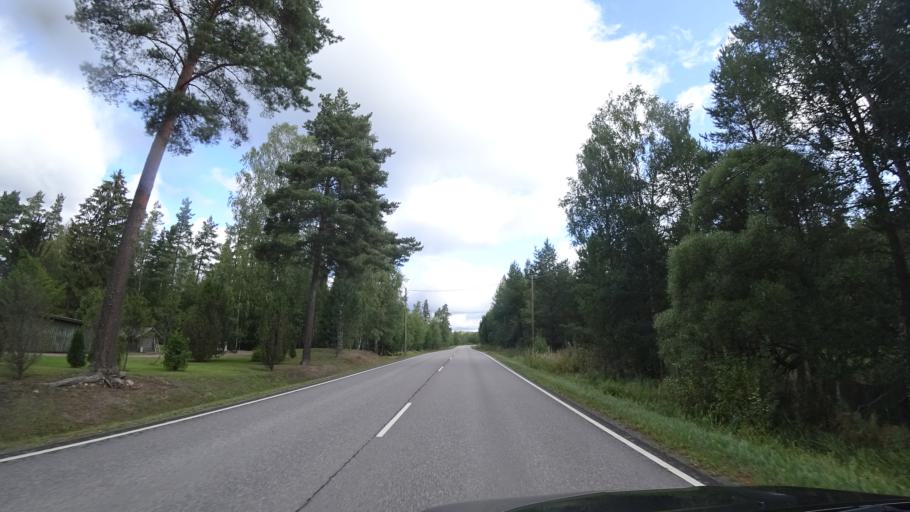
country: FI
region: Uusimaa
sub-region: Helsinki
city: Hyvinge
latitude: 60.6264
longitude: 25.0045
